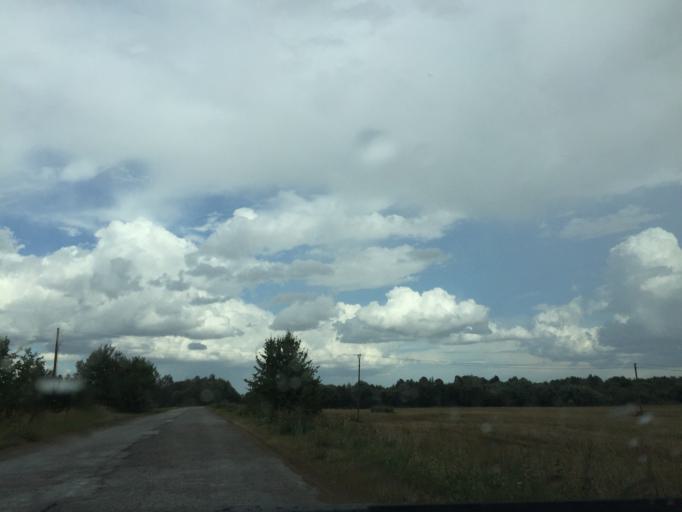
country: LV
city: Tervete
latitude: 56.3667
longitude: 23.4939
